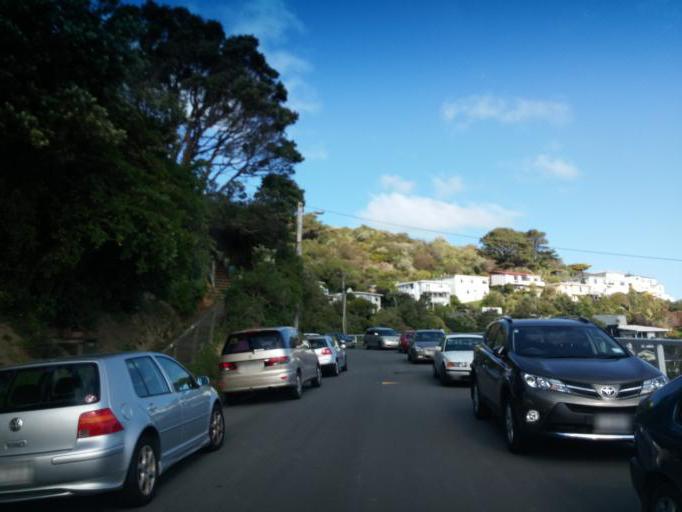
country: NZ
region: Wellington
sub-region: Wellington City
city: Wellington
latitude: -41.3177
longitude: 174.8227
